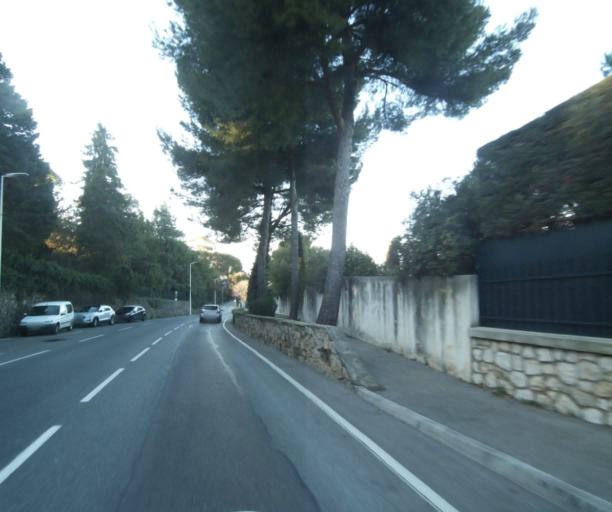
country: FR
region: Provence-Alpes-Cote d'Azur
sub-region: Departement des Alpes-Maritimes
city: Antibes
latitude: 43.5635
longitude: 7.1260
